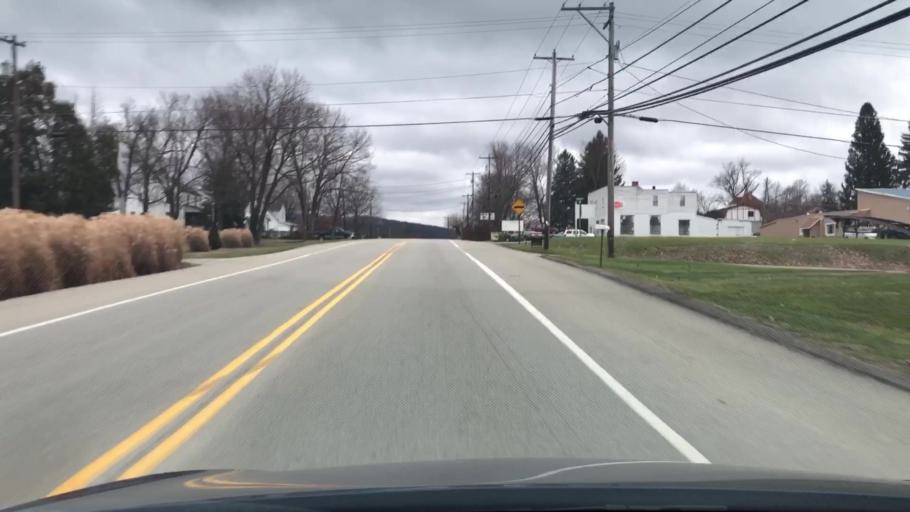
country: US
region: Pennsylvania
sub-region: Fayette County
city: Connellsville
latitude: 40.0292
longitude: -79.5812
